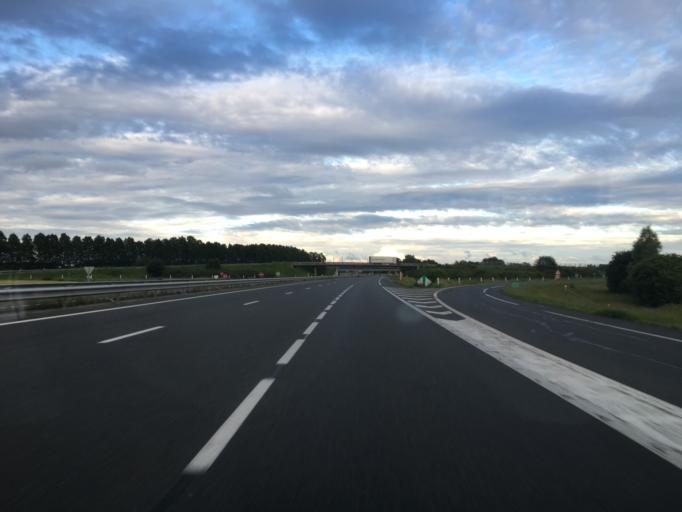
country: FR
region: Ile-de-France
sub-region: Departement de Seine-et-Marne
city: Moisenay
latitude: 48.5863
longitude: 2.7231
